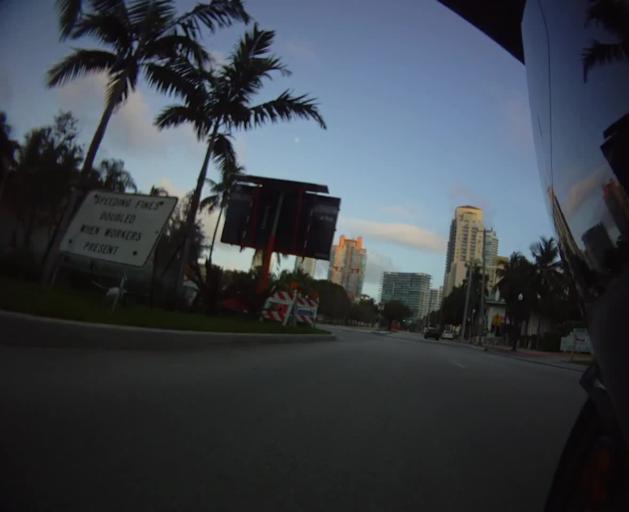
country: US
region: Florida
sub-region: Miami-Dade County
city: Miami Beach
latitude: 25.7726
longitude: -80.1397
